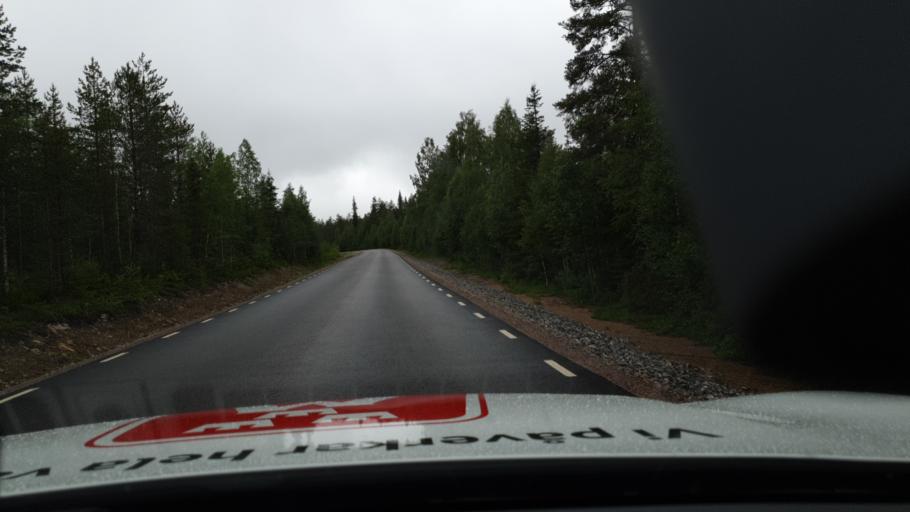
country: SE
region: Norrbotten
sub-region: Overtornea Kommun
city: OEvertornea
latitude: 66.4359
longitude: 23.5102
